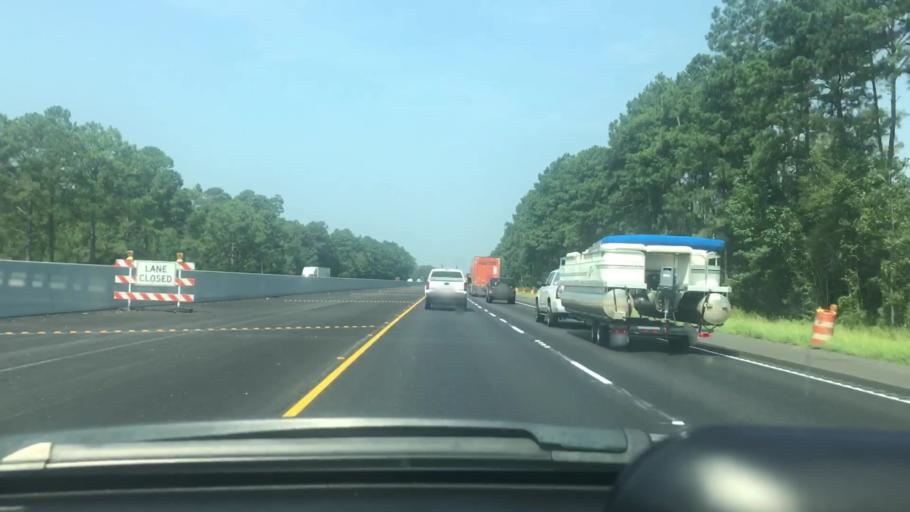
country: US
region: Louisiana
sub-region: Livingston Parish
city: Livingston
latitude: 30.4747
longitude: -90.6659
